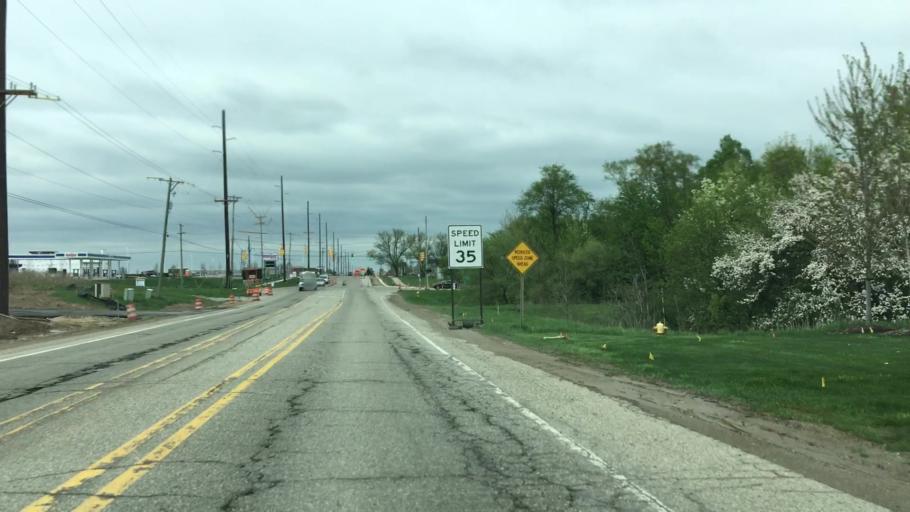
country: US
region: Michigan
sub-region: Ottawa County
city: Hudsonville
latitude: 42.8390
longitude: -85.8618
